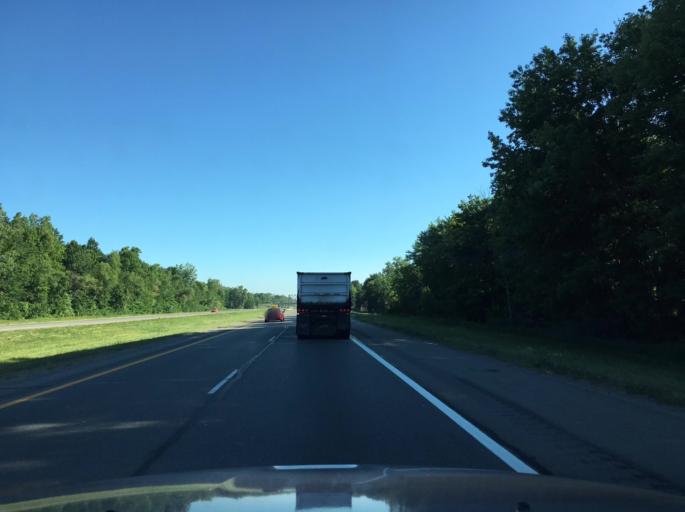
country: US
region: Michigan
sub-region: Macomb County
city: Shelby
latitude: 42.6625
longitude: -83.0143
